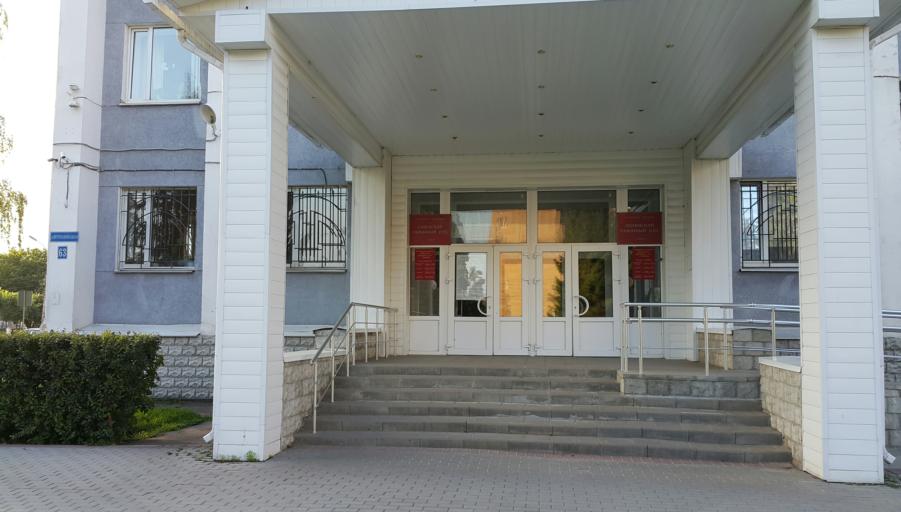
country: RU
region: Tambov
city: Tambov
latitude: 52.7203
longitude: 41.4386
